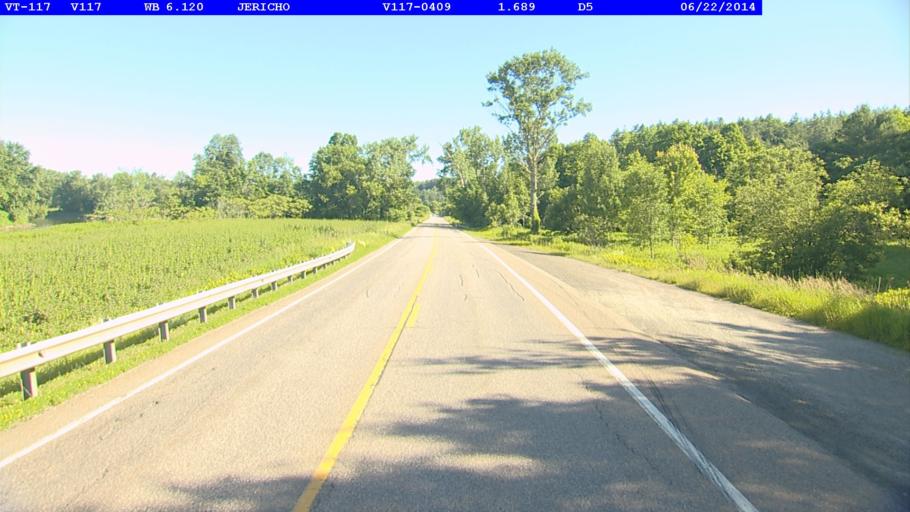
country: US
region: Vermont
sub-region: Chittenden County
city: Williston
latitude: 44.4509
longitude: -73.0179
